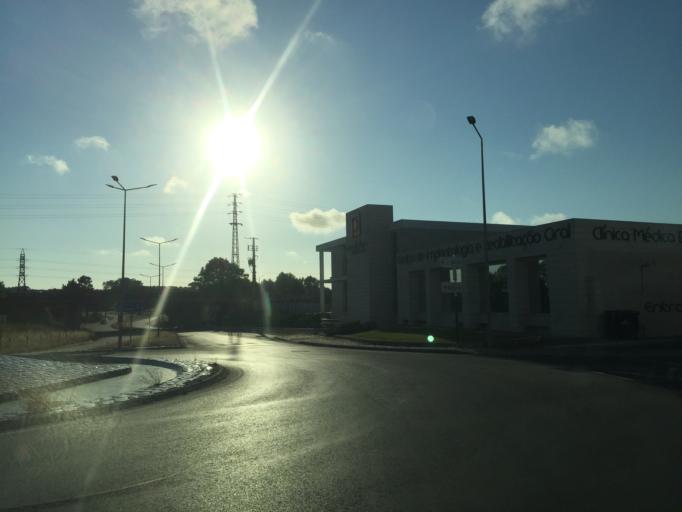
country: PT
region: Leiria
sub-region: Caldas da Rainha
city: Caldas da Rainha
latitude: 39.4065
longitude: -9.1528
